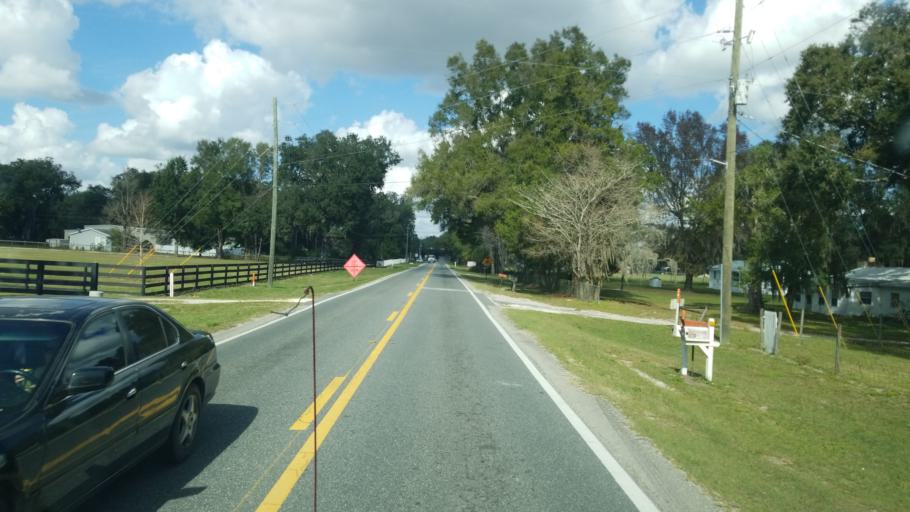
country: US
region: Florida
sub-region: Marion County
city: Belleview
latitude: 29.0081
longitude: -82.1199
